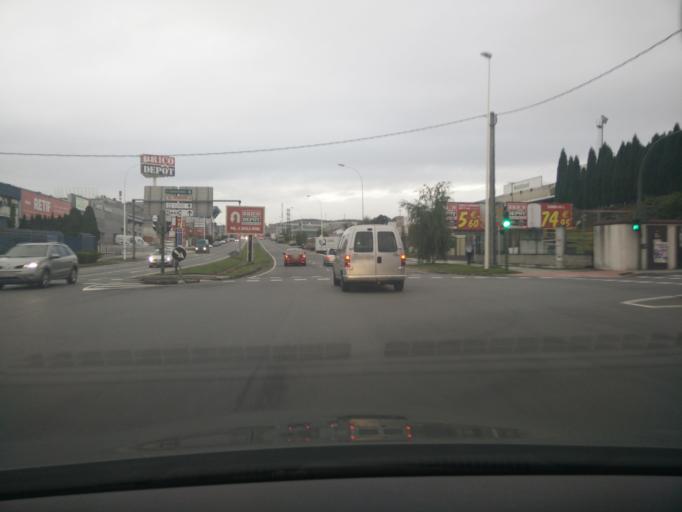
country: ES
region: Galicia
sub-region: Provincia da Coruna
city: A Coruna
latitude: 43.3505
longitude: -8.4229
